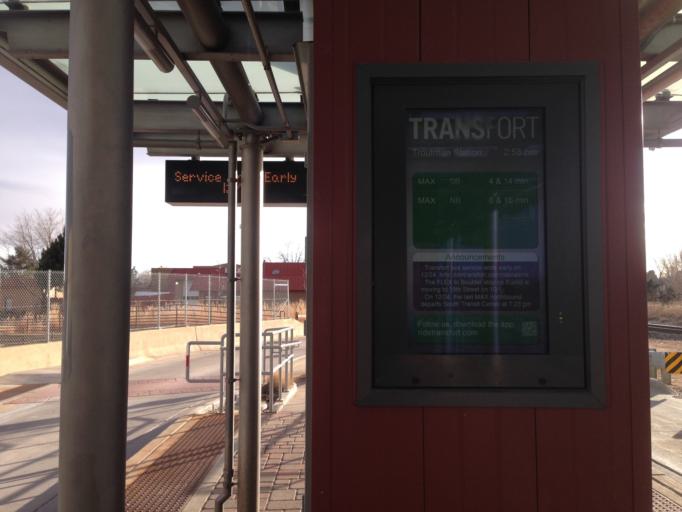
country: US
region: Colorado
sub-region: Larimer County
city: Fort Collins
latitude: 40.5290
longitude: -105.0806
